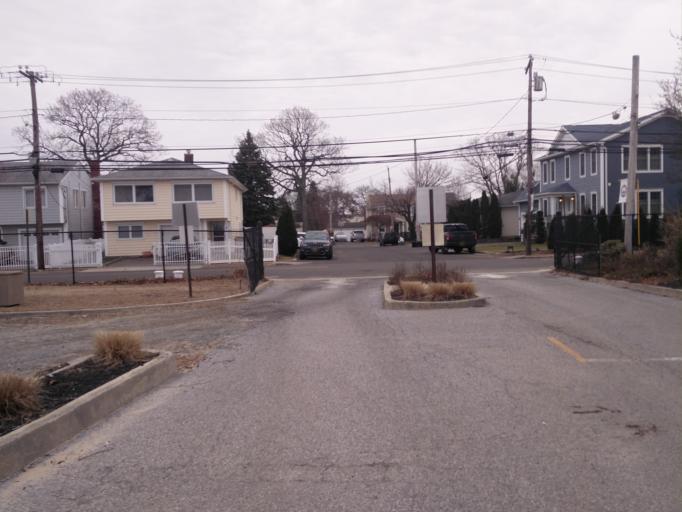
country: US
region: New York
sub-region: Nassau County
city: Bayville
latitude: 40.9092
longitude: -73.5420
